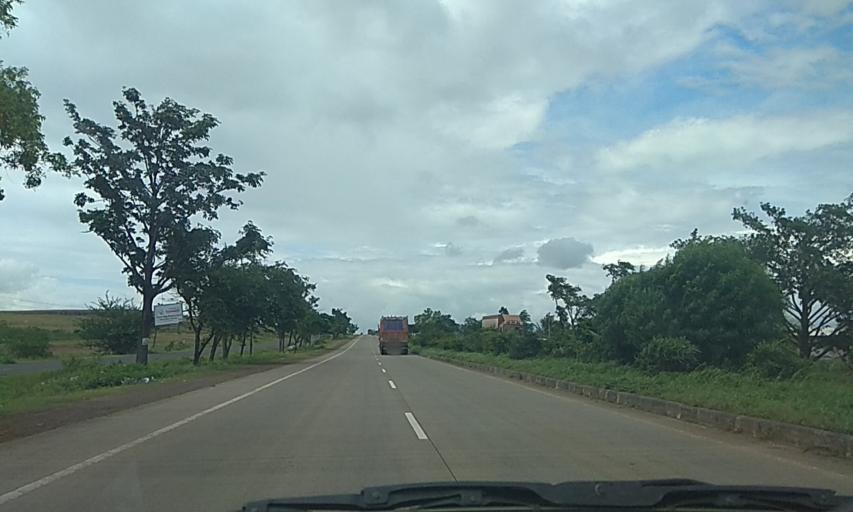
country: IN
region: Maharashtra
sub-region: Kolhapur
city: Kagal
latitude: 16.5200
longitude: 74.3260
